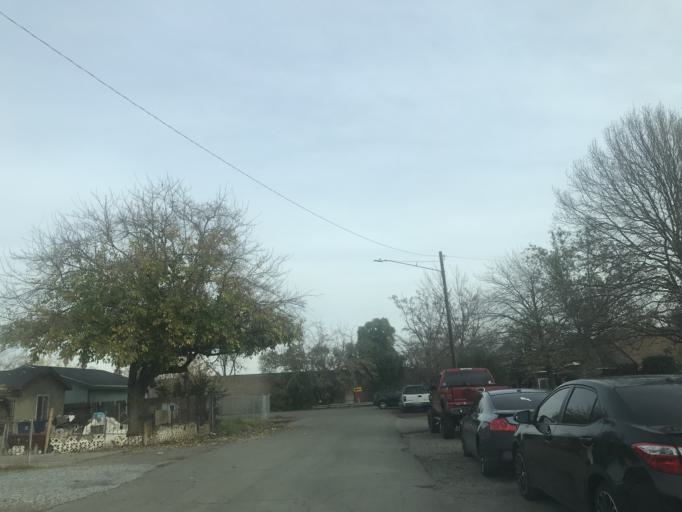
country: US
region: California
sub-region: Sacramento County
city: Parkway
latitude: 38.5272
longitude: -121.4701
